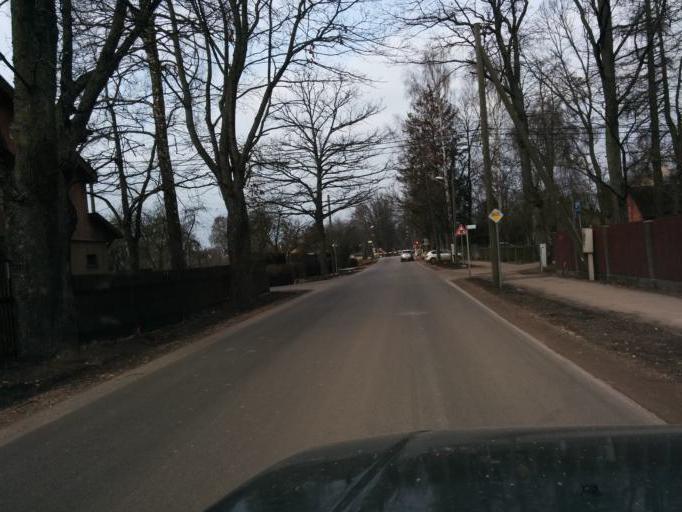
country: LV
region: Jurmala
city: Jurmala
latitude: 56.9582
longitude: 23.7231
